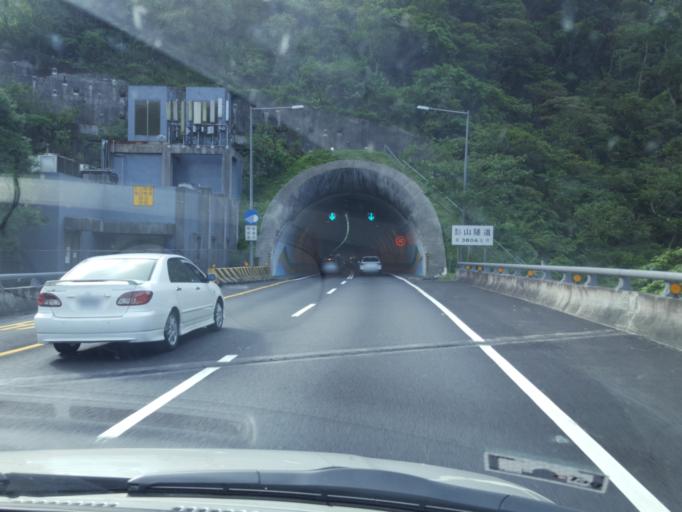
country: TW
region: Taiwan
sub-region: Keelung
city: Keelung
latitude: 24.9495
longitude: 121.7016
